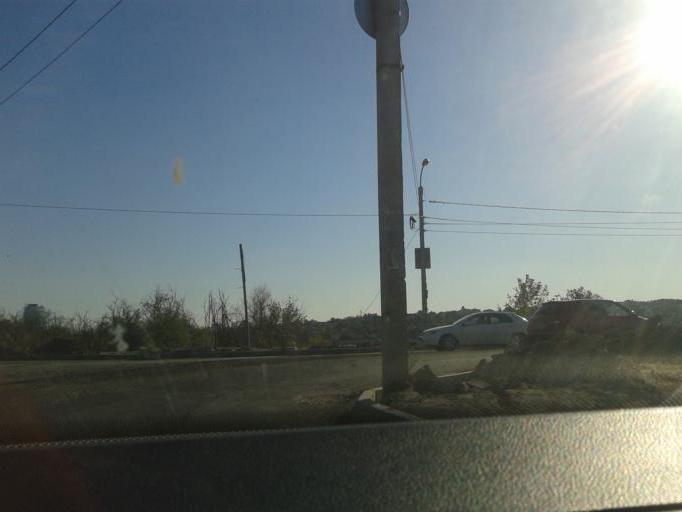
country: RU
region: Volgograd
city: Volgograd
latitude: 48.7453
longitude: 44.5244
